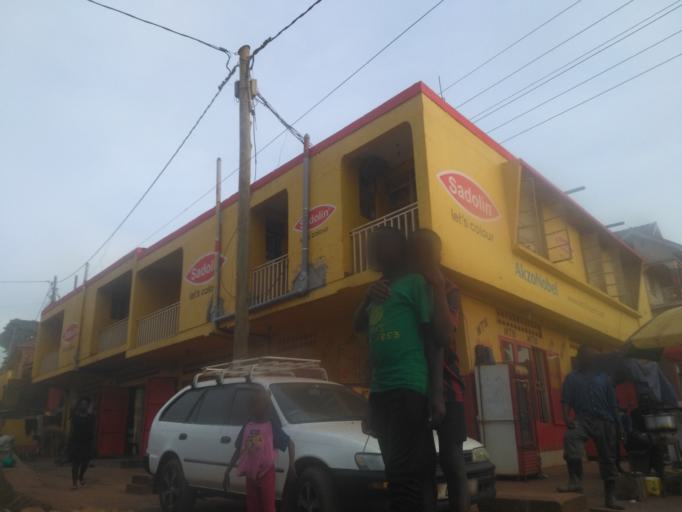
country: UG
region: Central Region
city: Kampala Central Division
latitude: 0.3465
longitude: 32.5723
